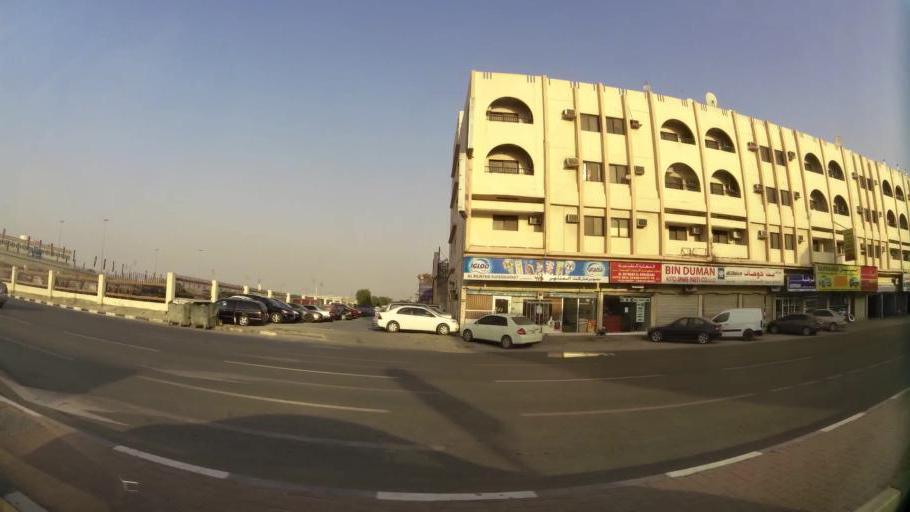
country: AE
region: Ash Shariqah
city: Sharjah
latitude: 25.3332
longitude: 55.4115
